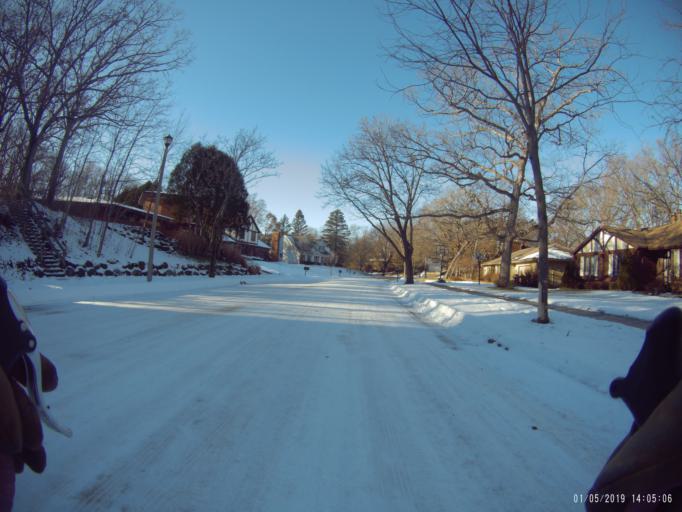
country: US
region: Wisconsin
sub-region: Dane County
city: Shorewood Hills
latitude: 43.0252
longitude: -89.4307
